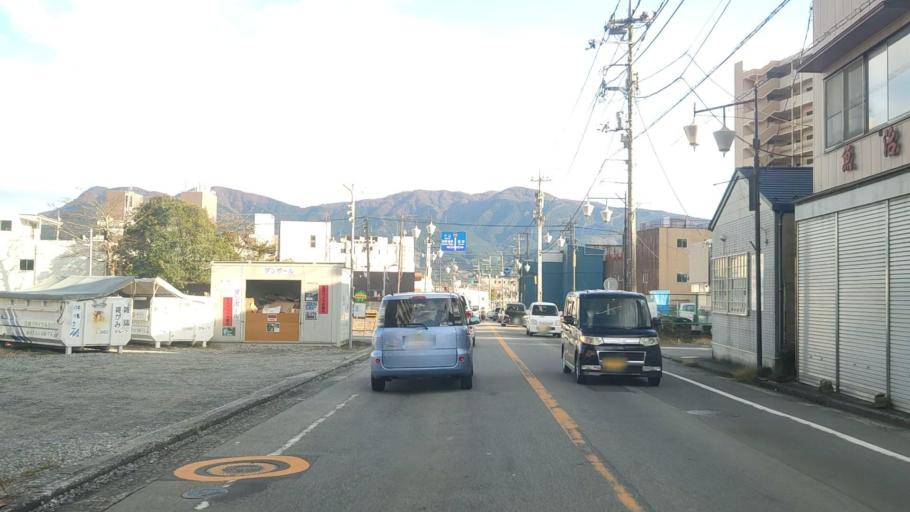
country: JP
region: Shizuoka
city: Gotemba
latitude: 35.3014
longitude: 138.9308
